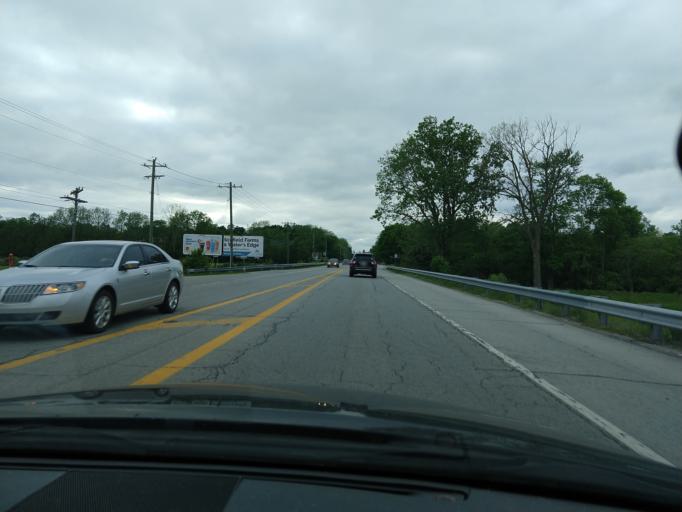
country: US
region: Indiana
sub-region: Hamilton County
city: Westfield
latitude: 40.0429
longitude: -86.1136
